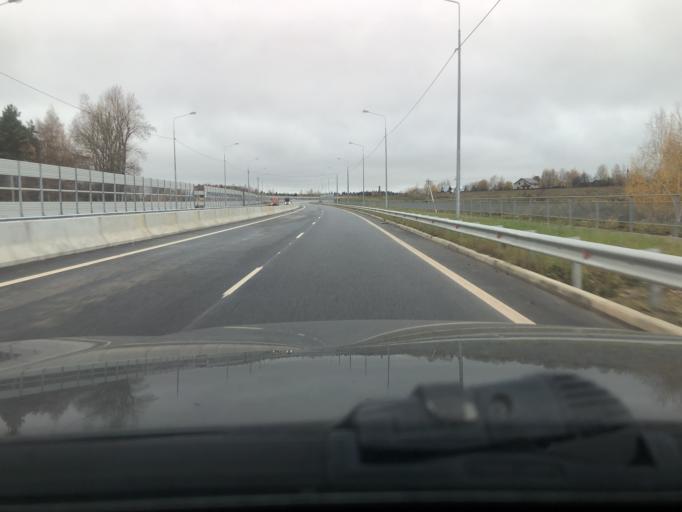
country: RU
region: Moskovskaya
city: Semkhoz
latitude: 56.3184
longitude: 38.0851
